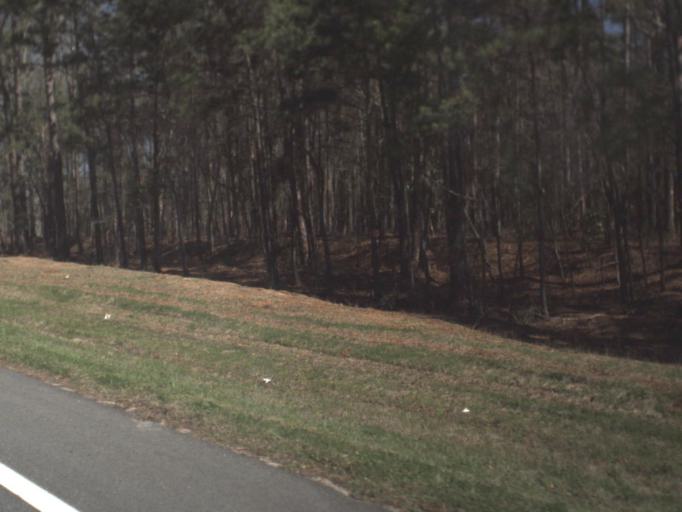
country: US
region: Florida
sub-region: Gadsden County
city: Quincy
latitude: 30.5120
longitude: -84.6094
